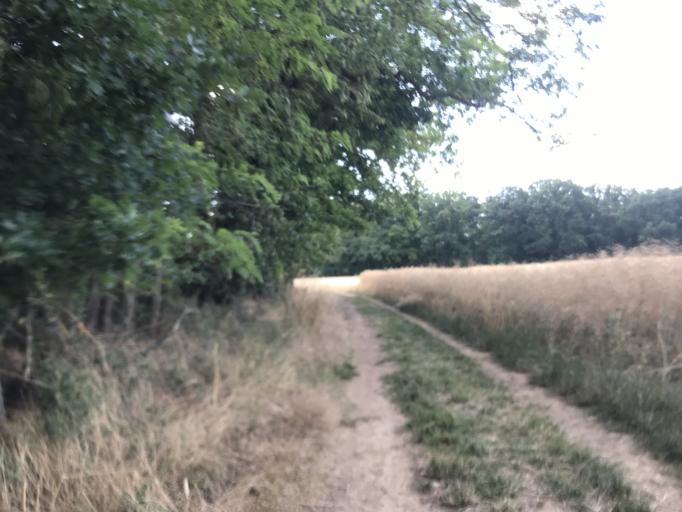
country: DE
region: Rheinland-Pfalz
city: Bubenheim
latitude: 49.9310
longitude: 8.0579
